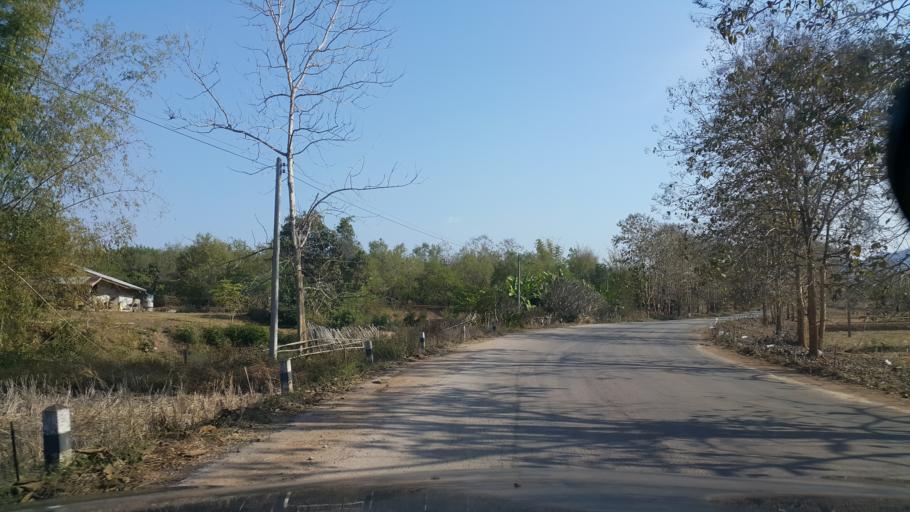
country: TH
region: Loei
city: Chiang Khan
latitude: 17.8497
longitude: 101.6462
